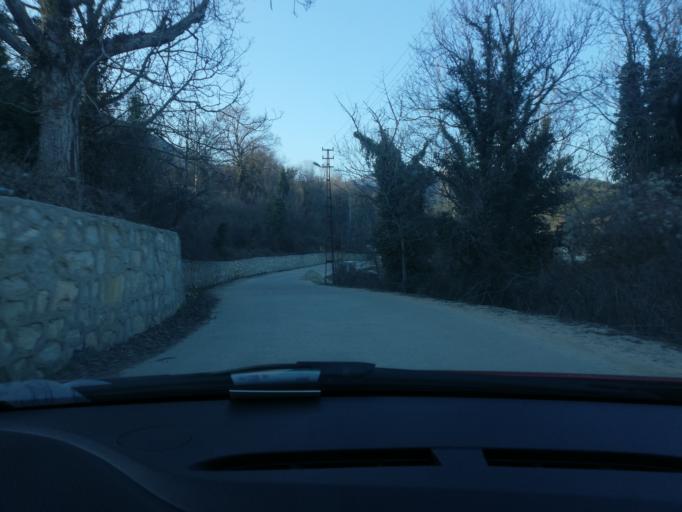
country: TR
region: Karabuk
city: Safranbolu
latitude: 41.2840
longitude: 32.6784
